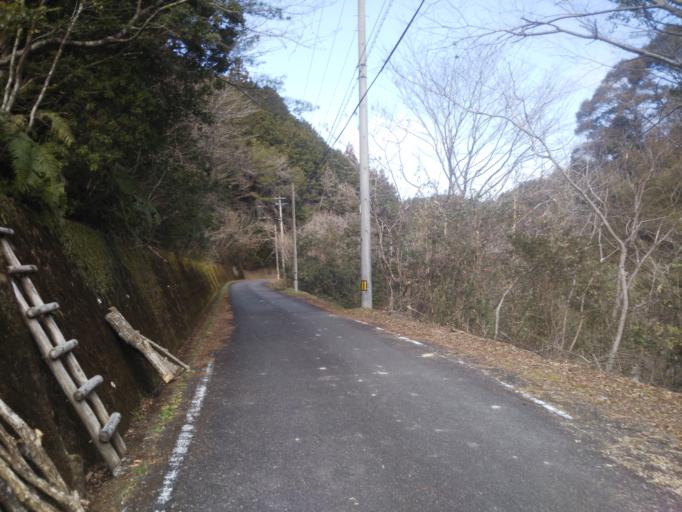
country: JP
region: Kochi
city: Nakamura
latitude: 33.0357
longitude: 132.9851
